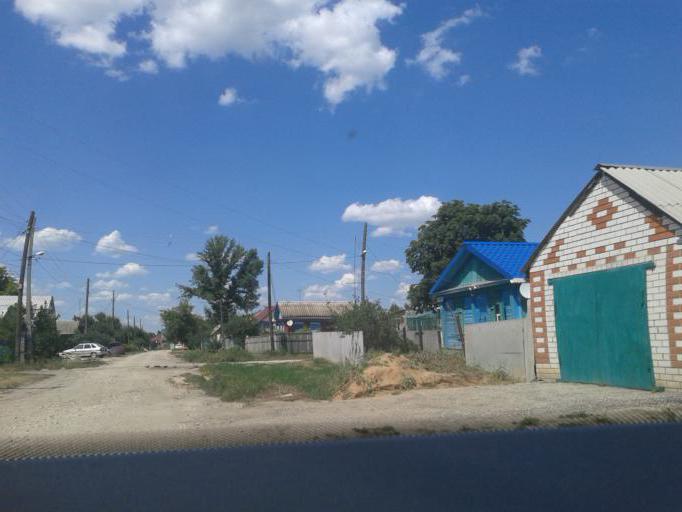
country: RU
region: Volgograd
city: Frolovo
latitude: 49.7615
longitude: 43.6618
